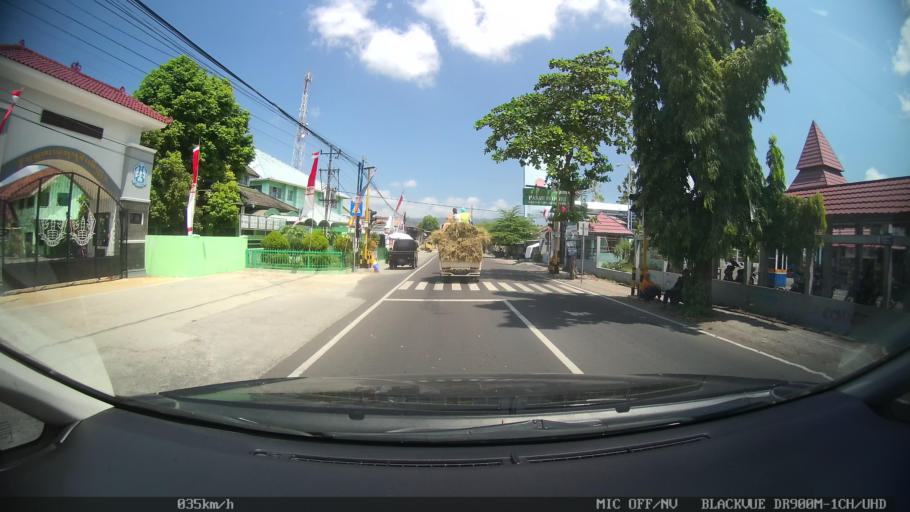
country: ID
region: Daerah Istimewa Yogyakarta
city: Sewon
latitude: -7.9176
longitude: 110.3820
